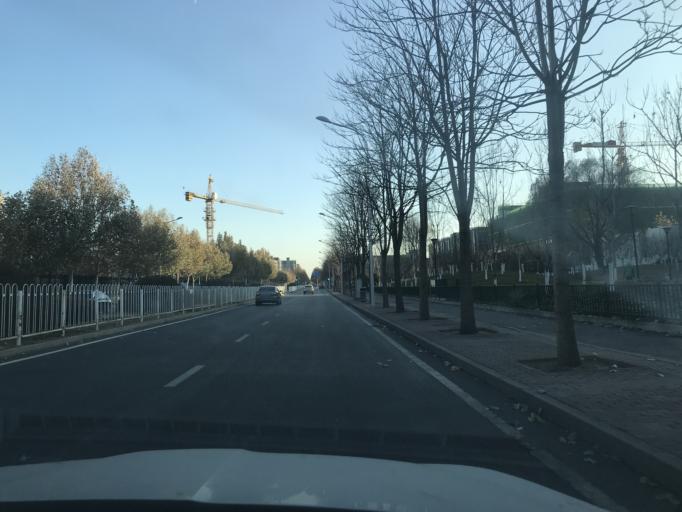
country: CN
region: Beijing
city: Xibeiwang
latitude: 40.0712
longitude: 116.2459
